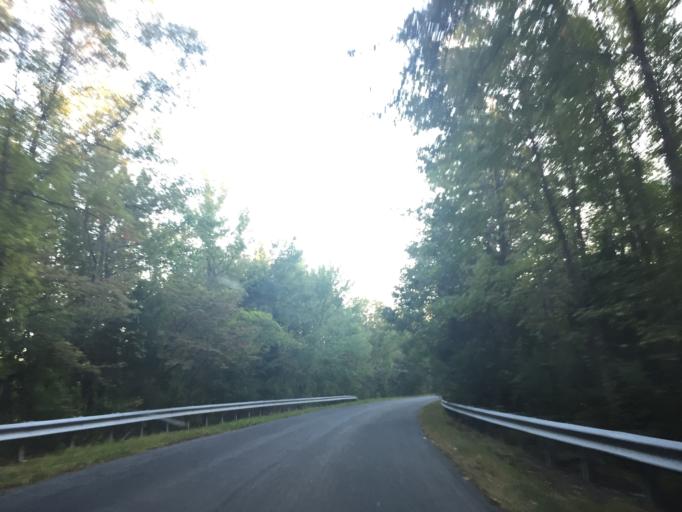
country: US
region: Maryland
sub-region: Baltimore County
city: Kingsville
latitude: 39.4272
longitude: -76.3883
